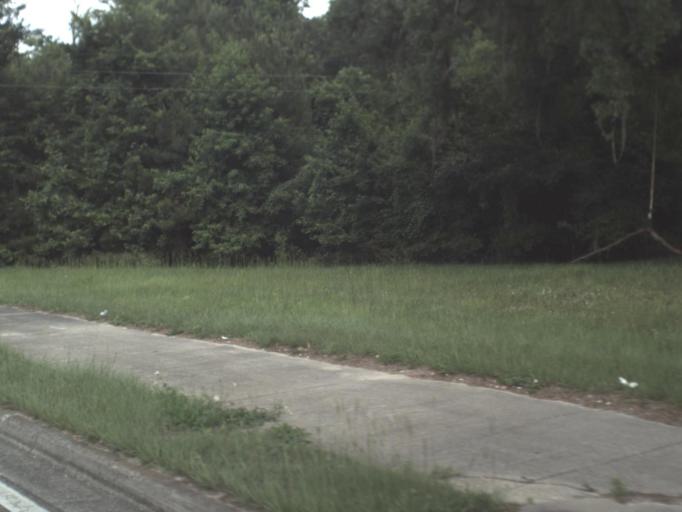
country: US
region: Florida
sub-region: Clay County
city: Middleburg
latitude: 30.0855
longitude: -81.8588
